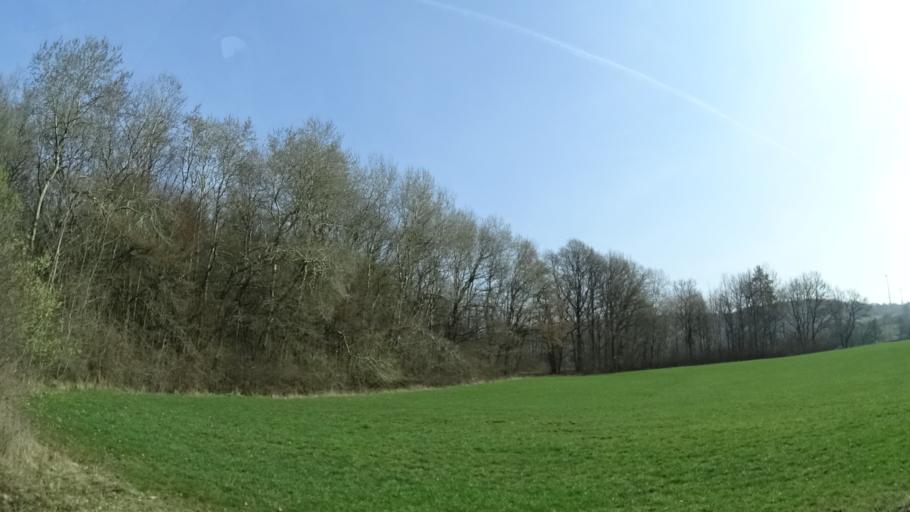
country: DE
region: Rheinland-Pfalz
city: Gimbweiler
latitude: 49.5754
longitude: 7.1823
